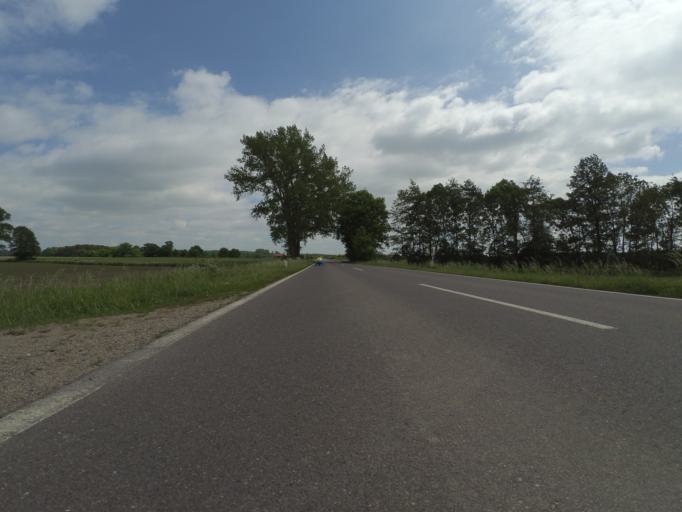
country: DE
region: Lower Saxony
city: Lehrte
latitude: 52.3967
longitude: 10.0083
